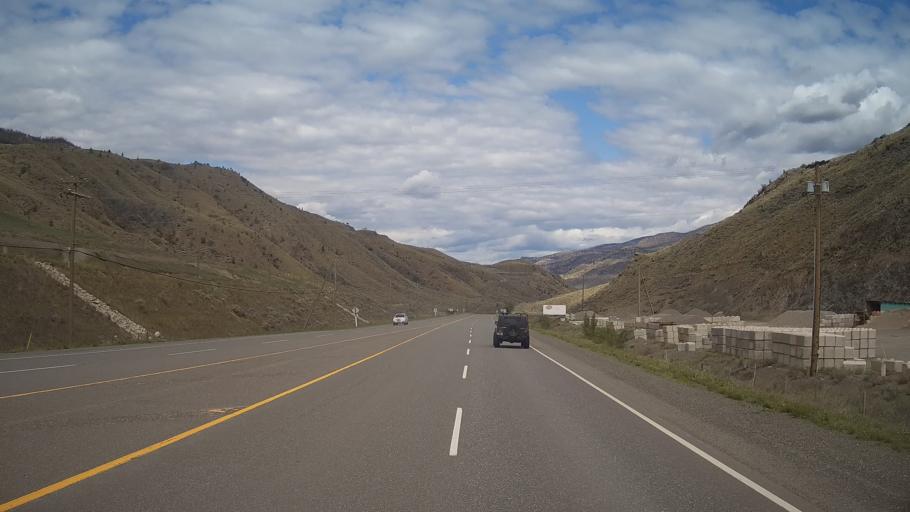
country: CA
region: British Columbia
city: Cache Creek
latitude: 50.7922
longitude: -121.3190
